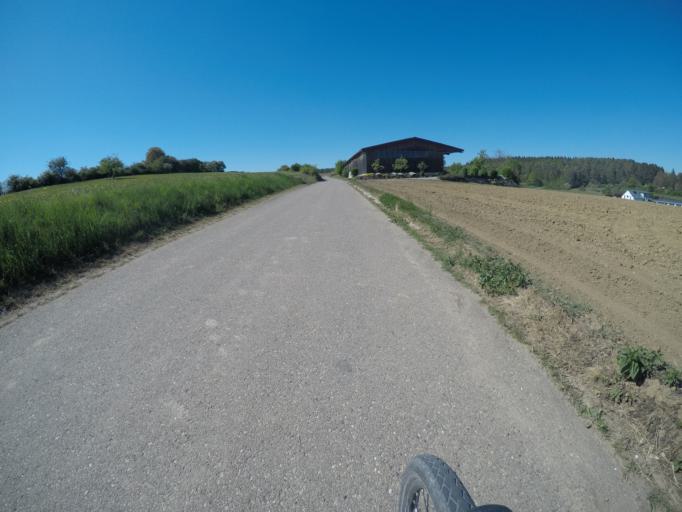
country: DE
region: Baden-Wuerttemberg
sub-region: Karlsruhe Region
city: Heimsheim
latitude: 48.8168
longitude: 8.8587
